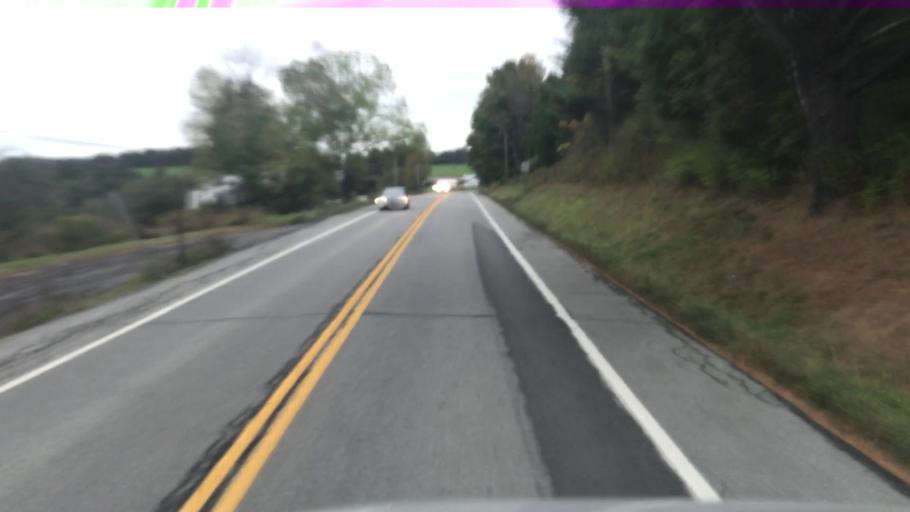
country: US
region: New York
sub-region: Otsego County
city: West End
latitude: 42.5312
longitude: -75.1764
